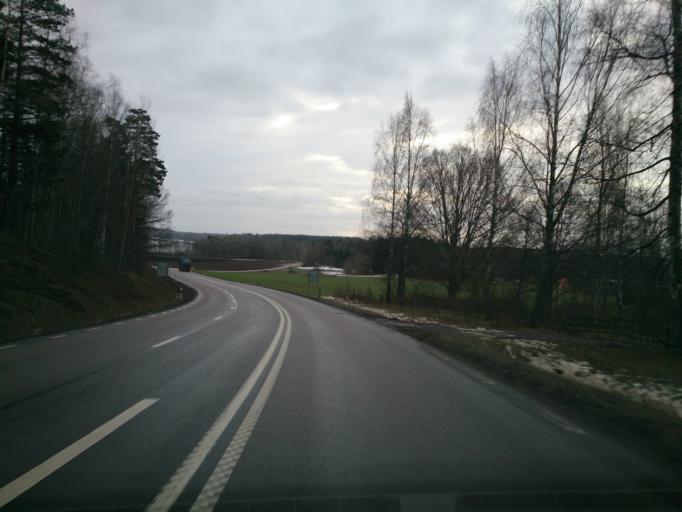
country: SE
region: OEstergoetland
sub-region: Atvidabergs Kommun
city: Atvidaberg
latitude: 58.2624
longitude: 15.9242
